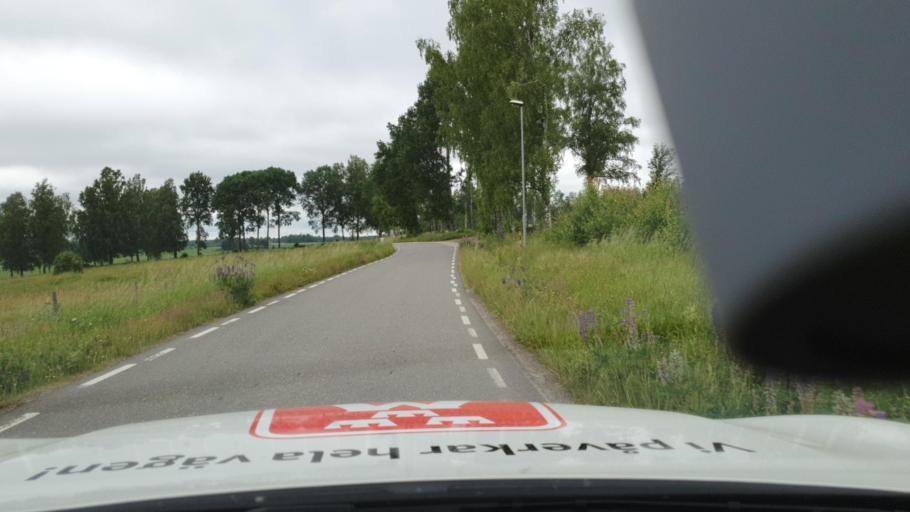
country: SE
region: Vaestra Goetaland
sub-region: Tibro Kommun
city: Tibro
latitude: 58.3887
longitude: 14.1871
